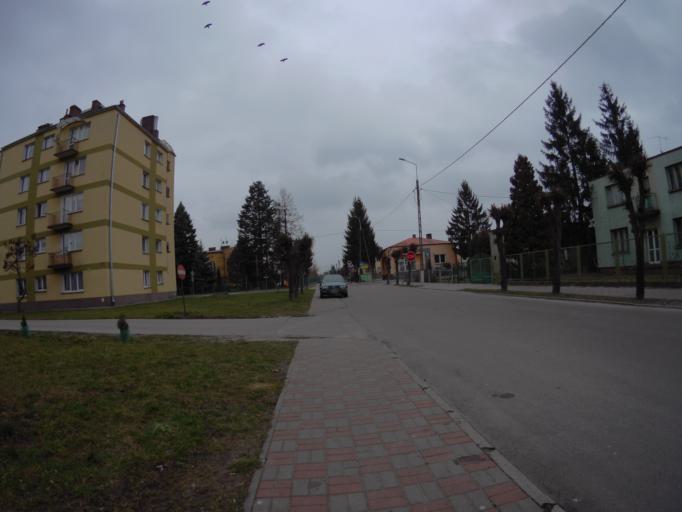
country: PL
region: Lublin Voivodeship
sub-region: Powiat bialski
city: Terespol
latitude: 52.0749
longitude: 23.6108
